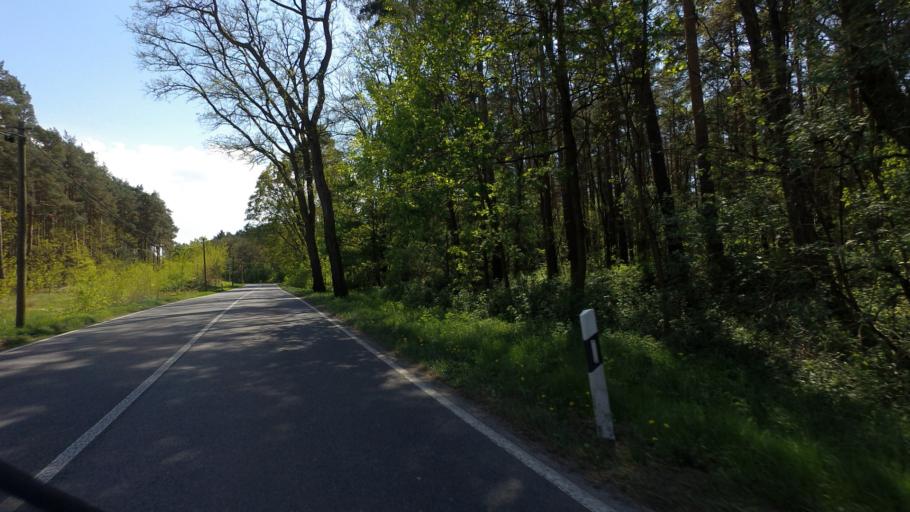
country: DE
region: Brandenburg
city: Lieberose
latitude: 51.9925
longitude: 14.2050
